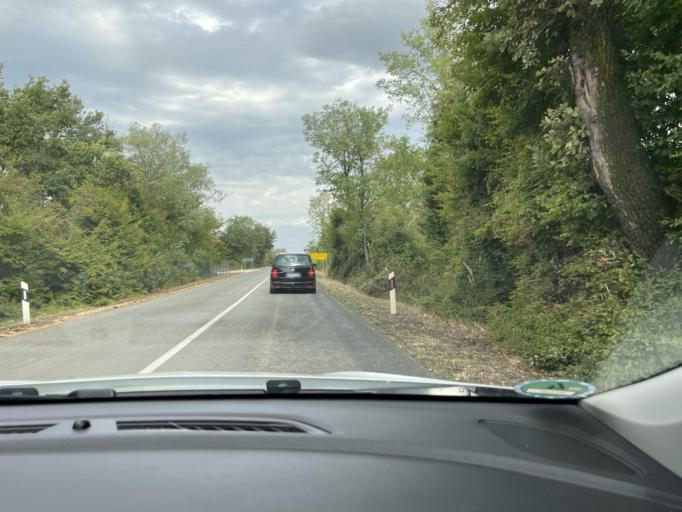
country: HR
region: Istarska
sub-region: Grad Porec
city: Porec
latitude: 45.2037
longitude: 13.6912
